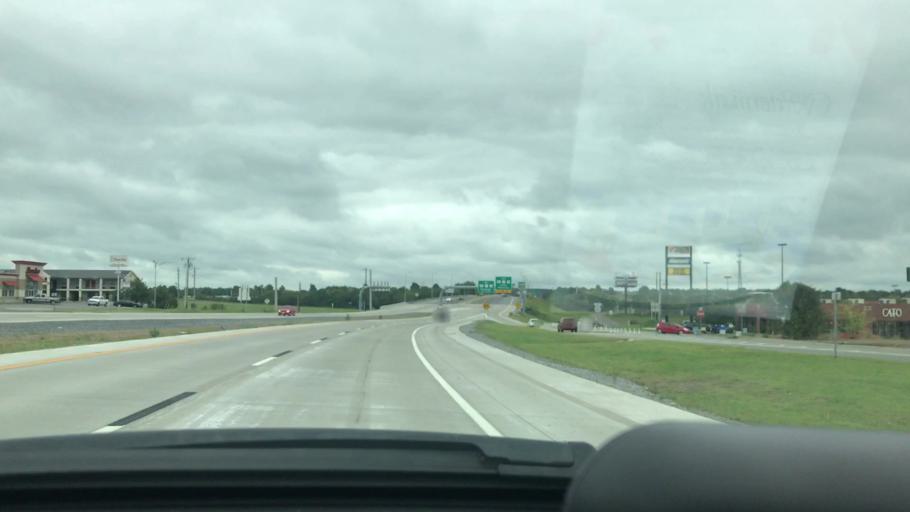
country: US
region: Oklahoma
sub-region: Pittsburg County
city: McAlester
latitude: 34.9196
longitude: -95.7448
